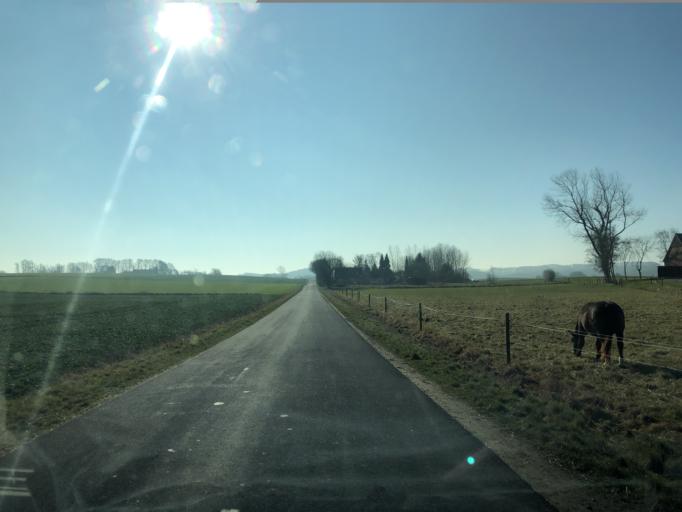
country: DK
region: Central Jutland
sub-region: Favrskov Kommune
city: Hammel
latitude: 56.2042
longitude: 9.8108
